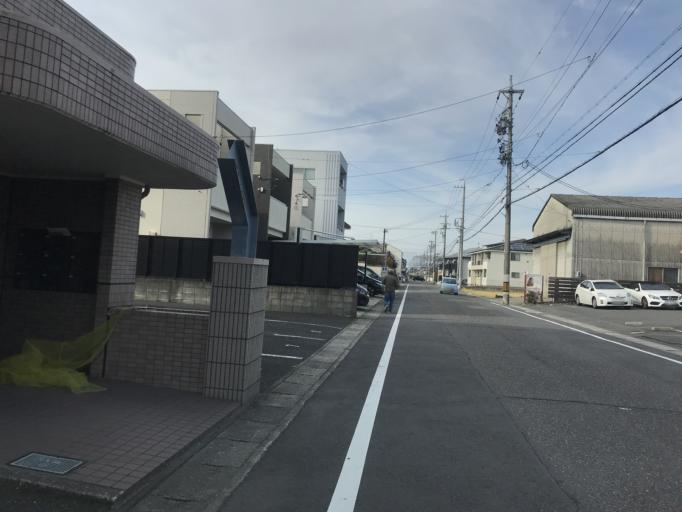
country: JP
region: Aichi
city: Inazawa
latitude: 35.2196
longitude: 136.8332
